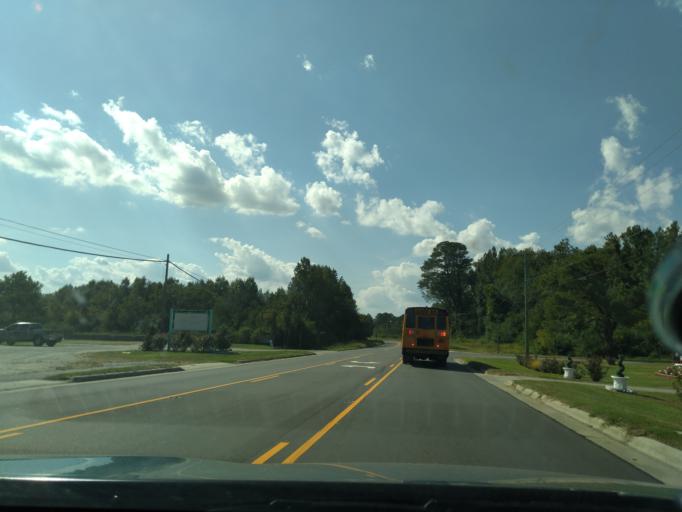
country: US
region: North Carolina
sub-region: Martin County
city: Robersonville
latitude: 35.8245
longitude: -77.2680
